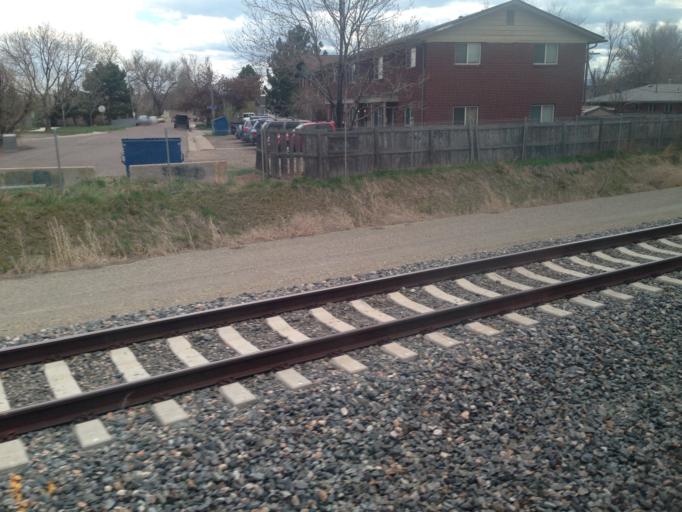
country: US
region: Colorado
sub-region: Jefferson County
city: Arvada
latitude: 39.7952
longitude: -105.0957
